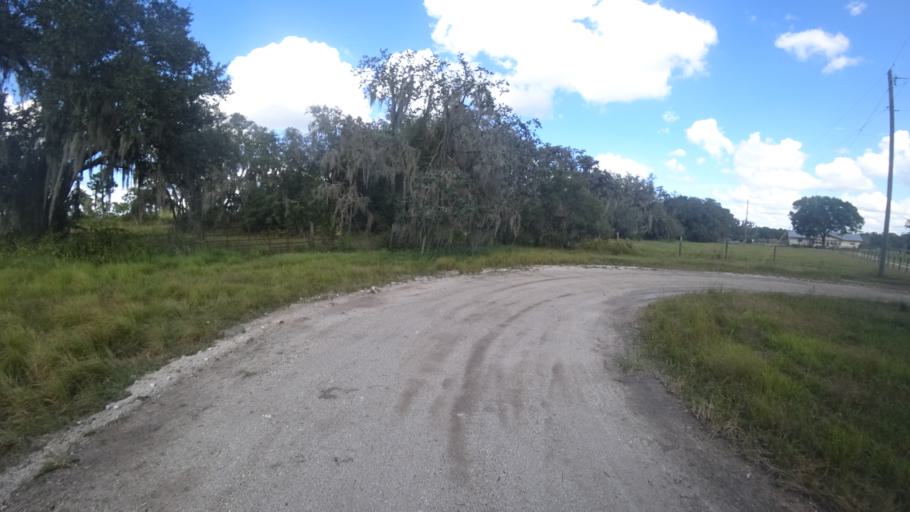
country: US
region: Florida
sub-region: Hillsborough County
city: Wimauma
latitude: 27.4372
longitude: -82.1455
